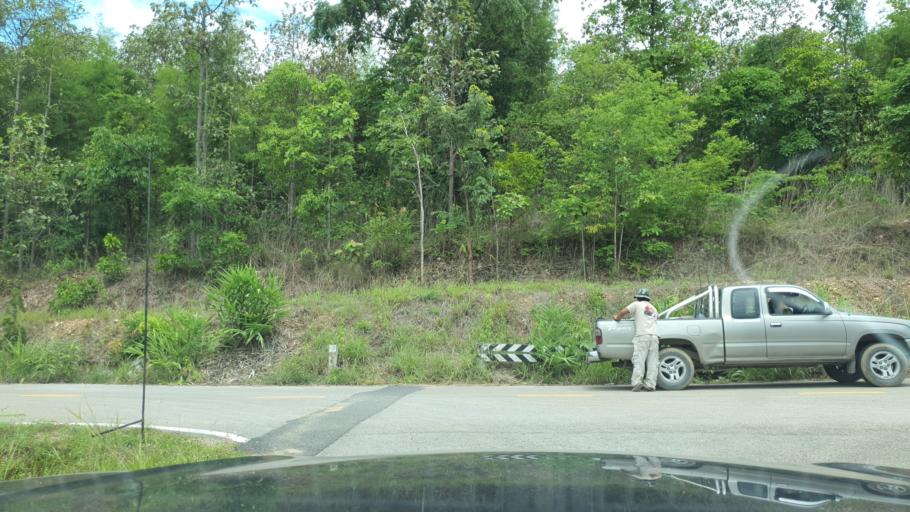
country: TH
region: Chiang Mai
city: San Sai
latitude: 18.9252
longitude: 99.0530
